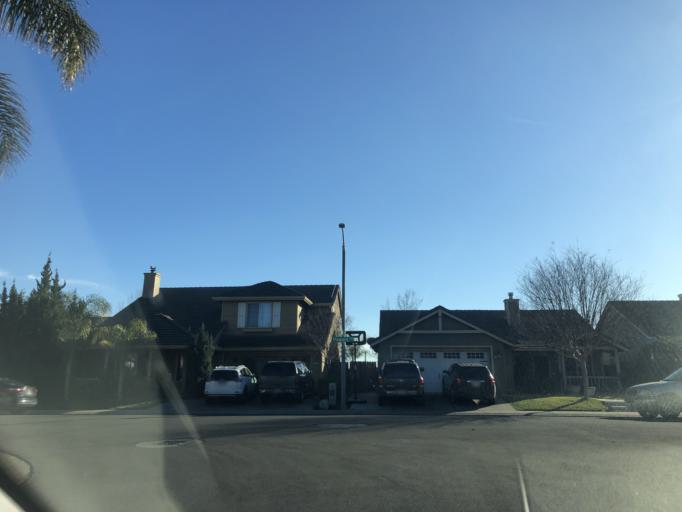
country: US
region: California
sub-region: Yolo County
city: Woodland
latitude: 38.6635
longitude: -121.7454
